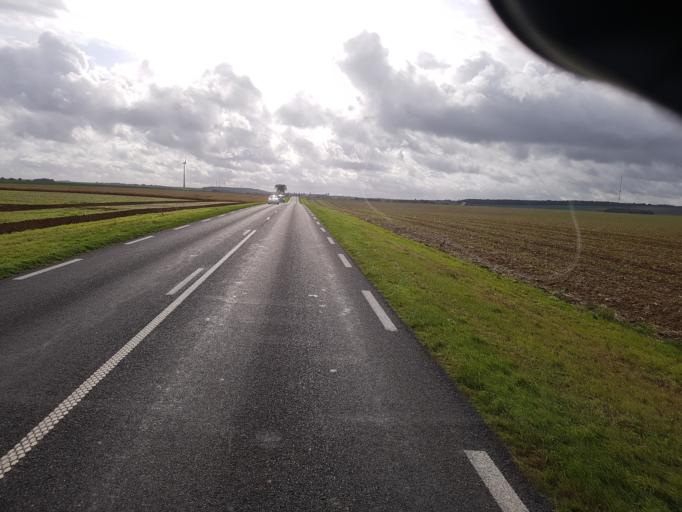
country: FR
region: Picardie
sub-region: Departement de l'Oise
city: Wavignies
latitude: 49.5344
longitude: 2.3867
